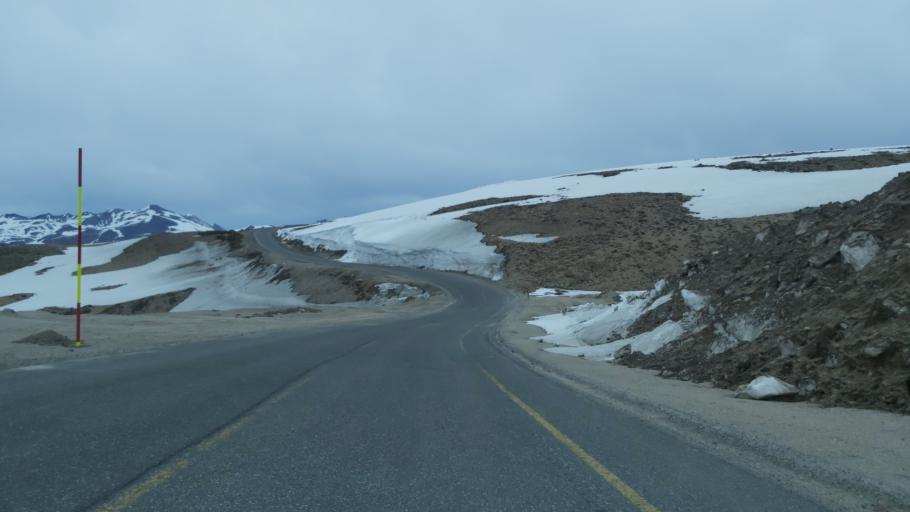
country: CL
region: Maule
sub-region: Provincia de Linares
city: Colbun
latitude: -36.0198
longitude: -70.5264
